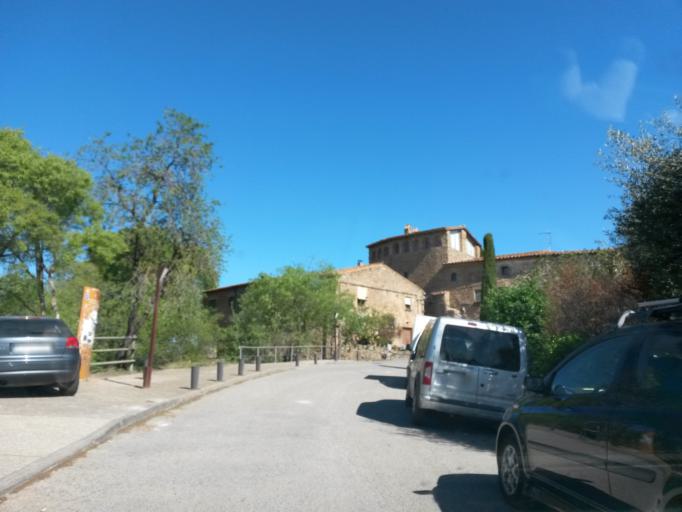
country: ES
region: Catalonia
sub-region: Provincia de Girona
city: Madremanya
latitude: 41.9899
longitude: 2.9556
